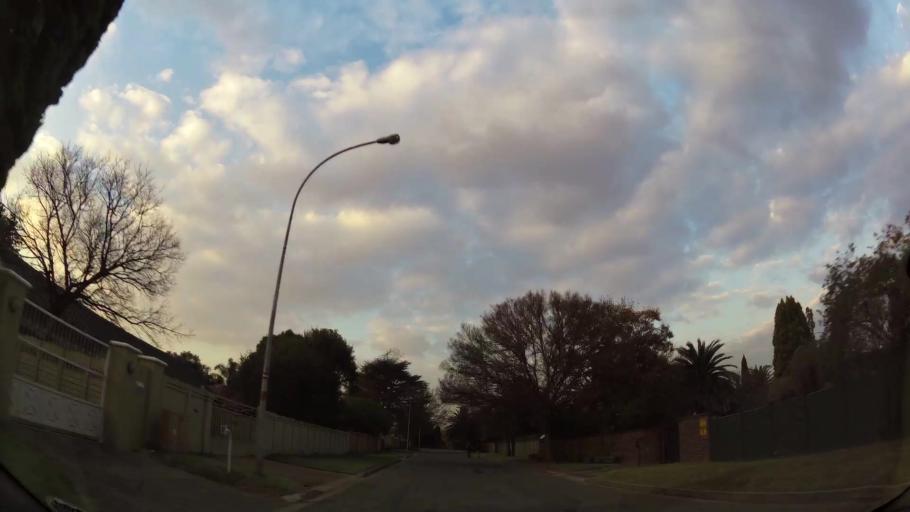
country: ZA
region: Gauteng
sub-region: Ekurhuleni Metropolitan Municipality
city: Benoni
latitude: -26.1751
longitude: 28.3050
